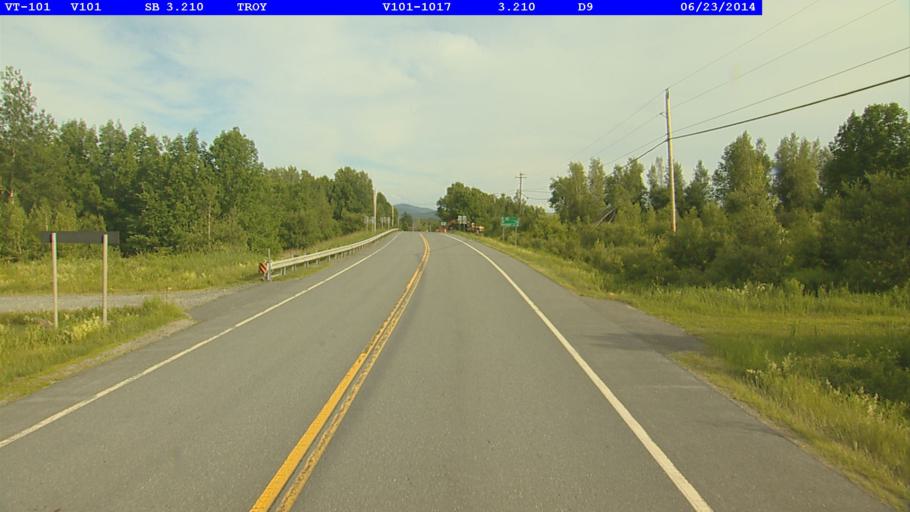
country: US
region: Vermont
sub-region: Orleans County
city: Newport
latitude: 44.9486
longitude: -72.4122
